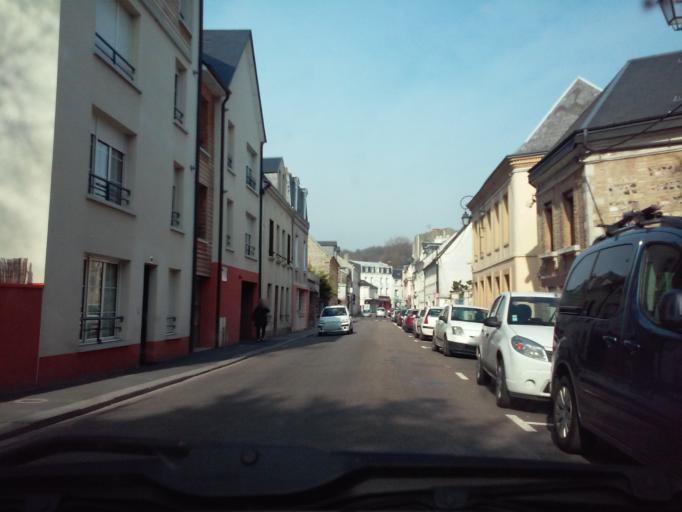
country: FR
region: Haute-Normandie
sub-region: Departement de la Seine-Maritime
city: Harfleur
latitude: 49.5059
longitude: 0.1964
